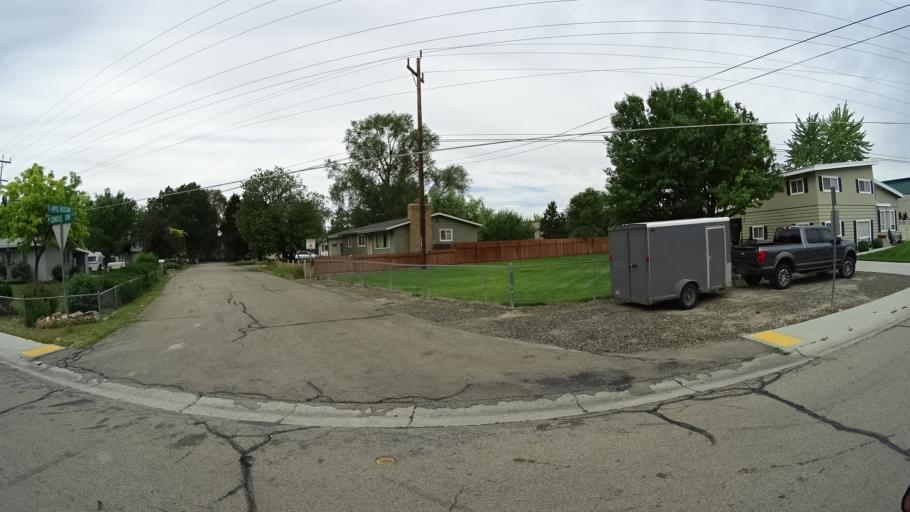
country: US
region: Idaho
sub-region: Ada County
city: Boise
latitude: 43.5728
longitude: -116.2121
